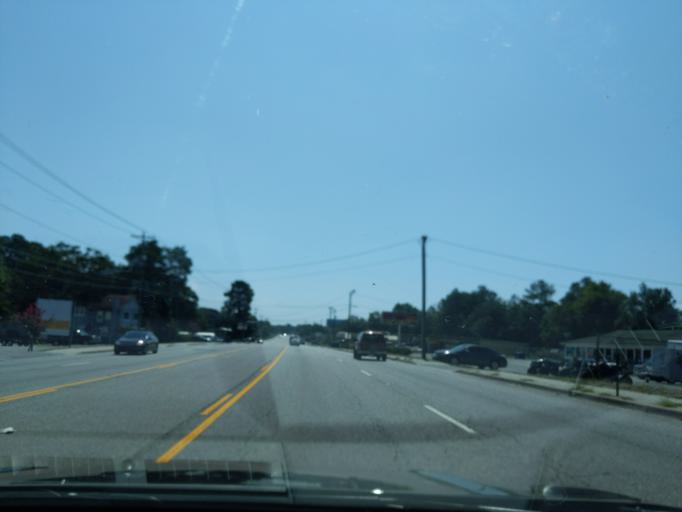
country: US
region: South Carolina
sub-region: Lexington County
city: Oak Grove
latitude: 33.9730
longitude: -81.1531
